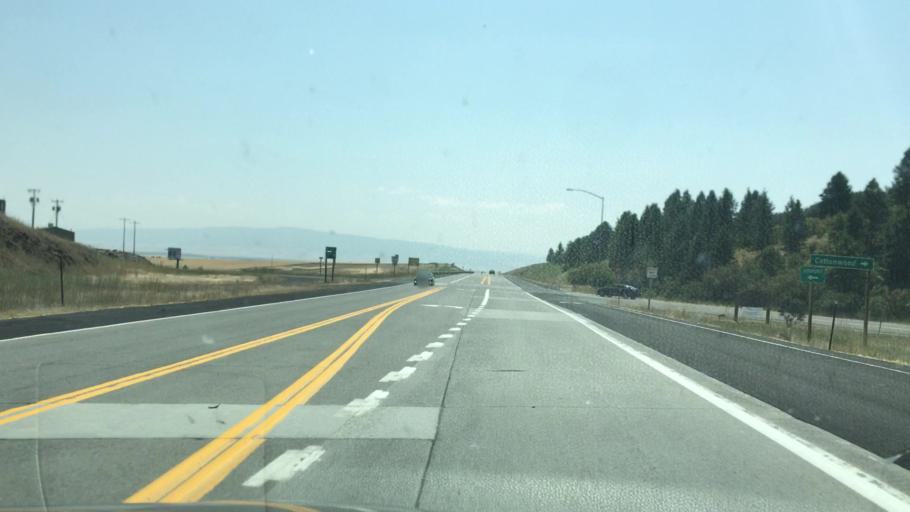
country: US
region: Idaho
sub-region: Lewis County
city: Nezperce
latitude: 46.0459
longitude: -116.3442
